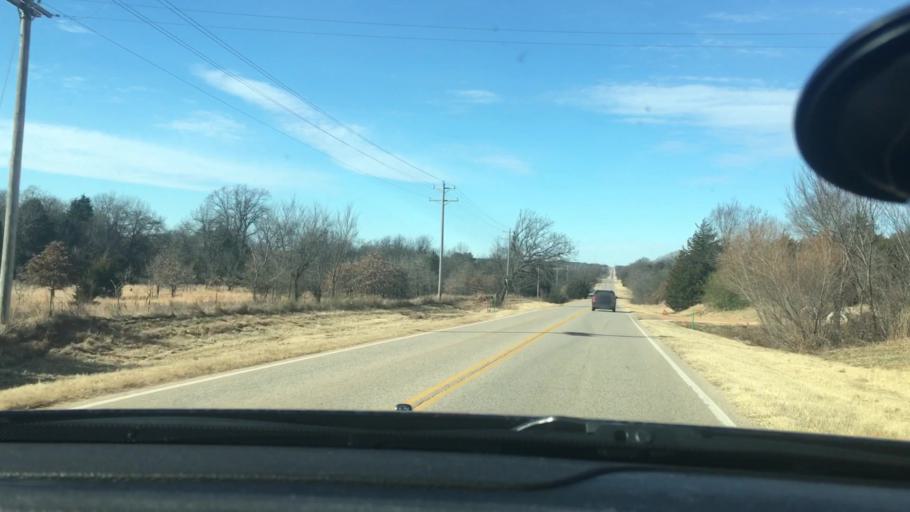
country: US
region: Oklahoma
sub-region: Cleveland County
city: Lexington
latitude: 35.0148
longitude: -97.1305
